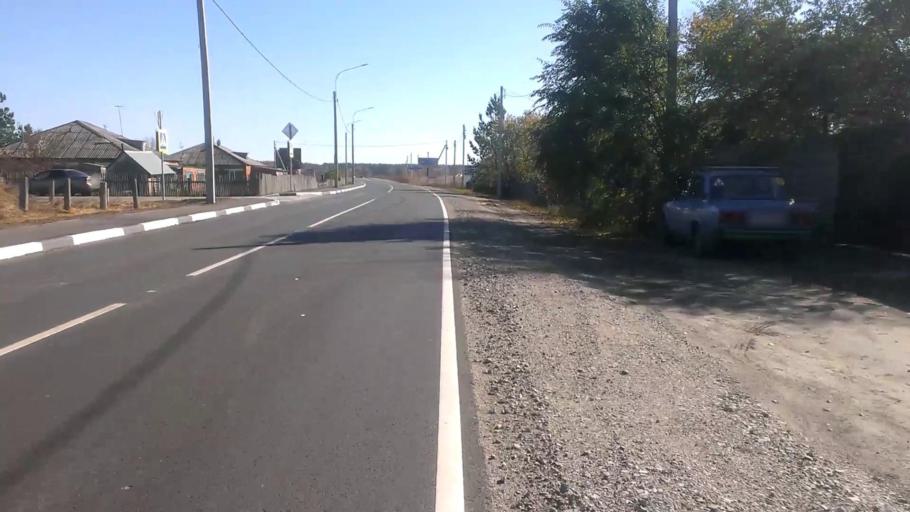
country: RU
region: Altai Krai
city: Sannikovo
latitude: 53.3150
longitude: 83.9600
